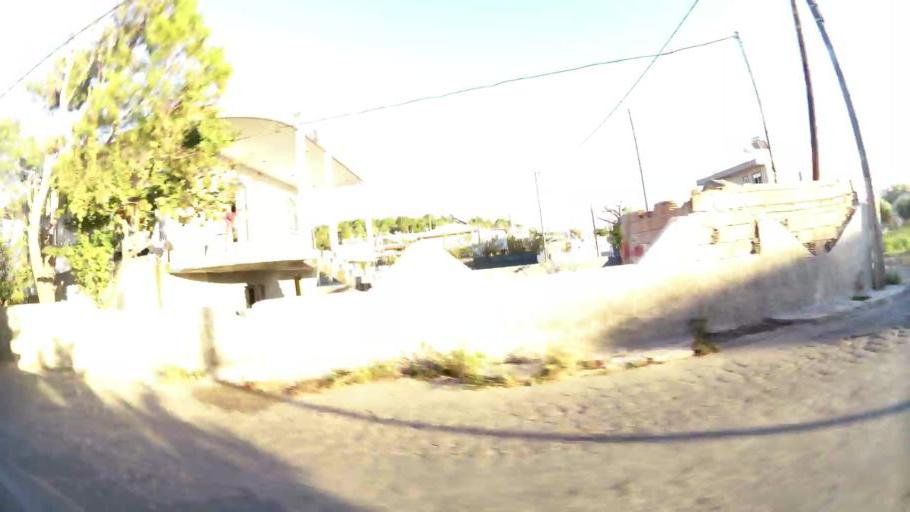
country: GR
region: Attica
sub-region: Nomarchia Anatolikis Attikis
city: Acharnes
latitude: 38.0899
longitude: 23.7169
